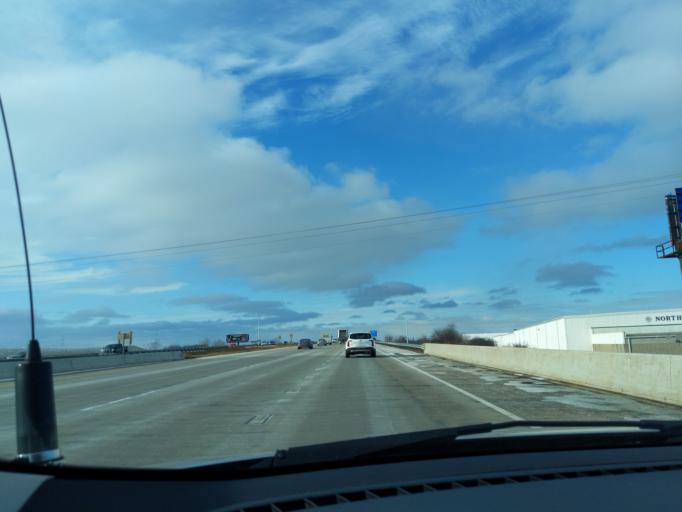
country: US
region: Wisconsin
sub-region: Brown County
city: Ashwaubenon
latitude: 44.4774
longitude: -88.0548
